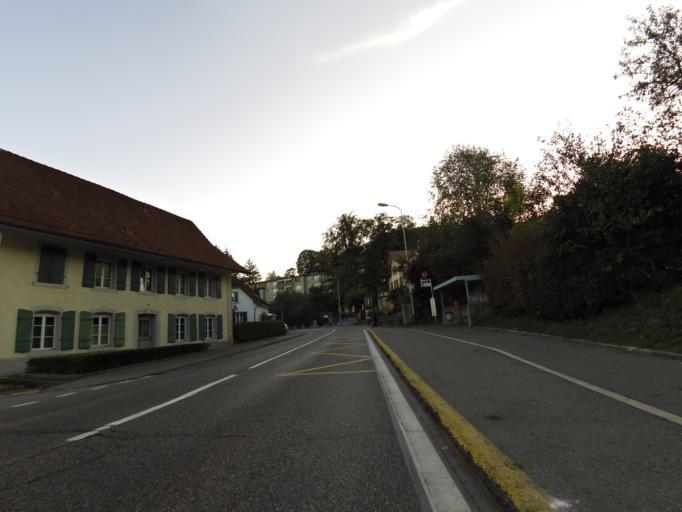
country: CH
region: Aargau
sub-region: Bezirk Aarau
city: Aarau
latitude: 47.4012
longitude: 8.0429
